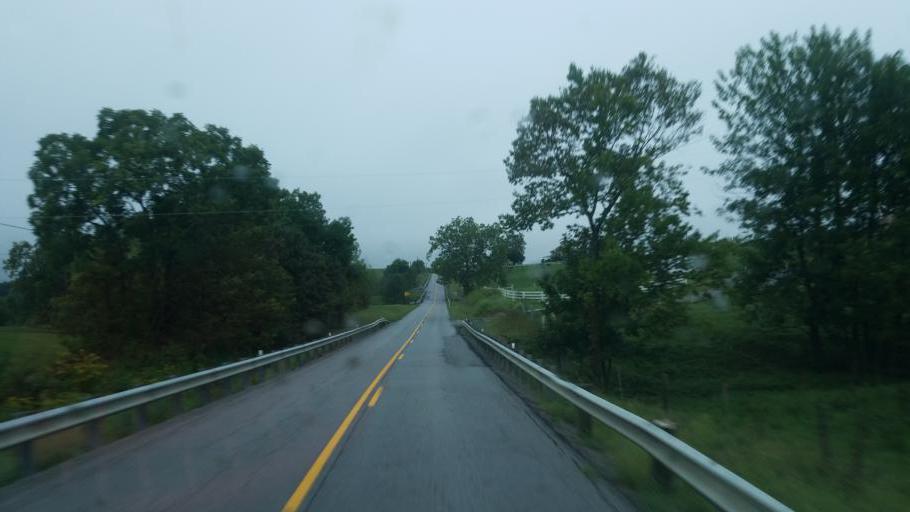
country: US
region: Kentucky
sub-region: Fleming County
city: Flemingsburg
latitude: 38.4139
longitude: -83.6787
